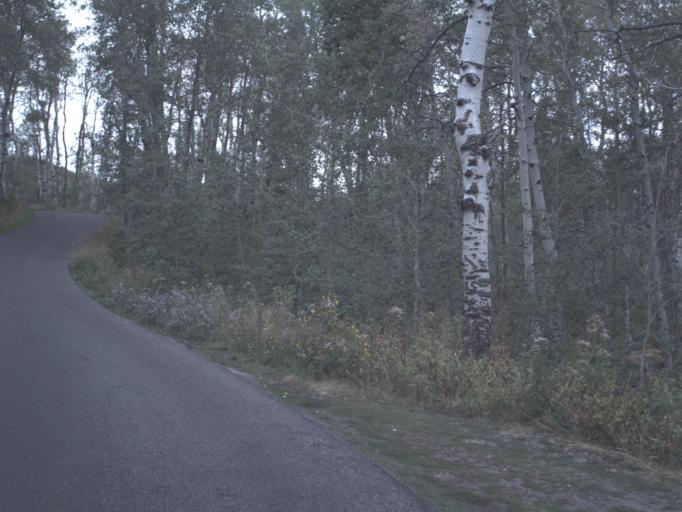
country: US
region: Utah
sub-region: Utah County
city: Lindon
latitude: 40.4263
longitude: -111.6072
